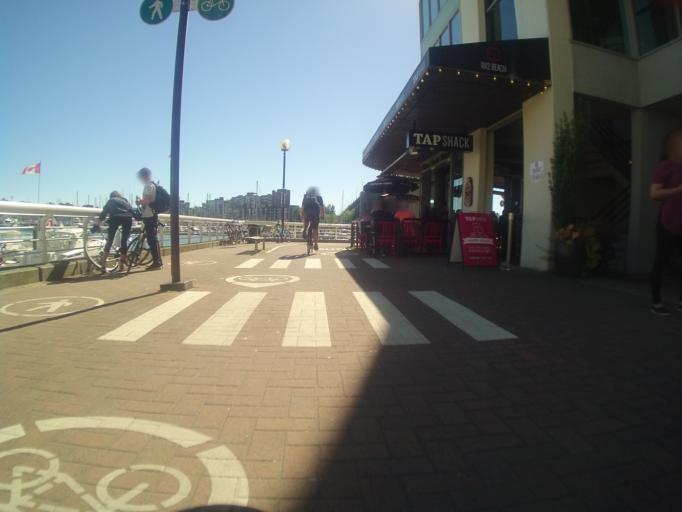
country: CA
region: British Columbia
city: West End
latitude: 49.2755
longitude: -123.1352
